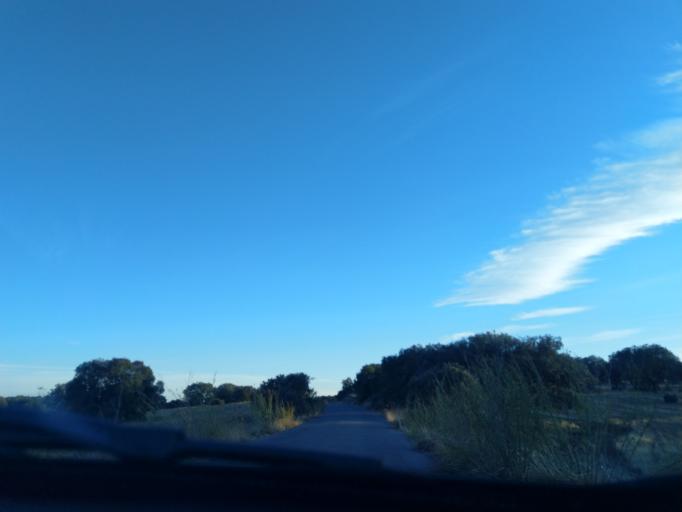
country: ES
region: Extremadura
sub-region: Provincia de Badajoz
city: Valverde de Llerena
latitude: 38.2377
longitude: -5.8238
